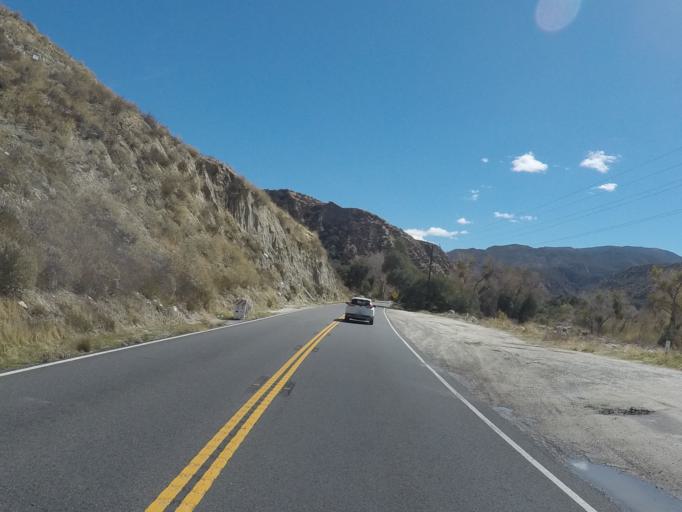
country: US
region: California
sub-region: Riverside County
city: Valle Vista
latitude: 33.7324
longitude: -116.8114
